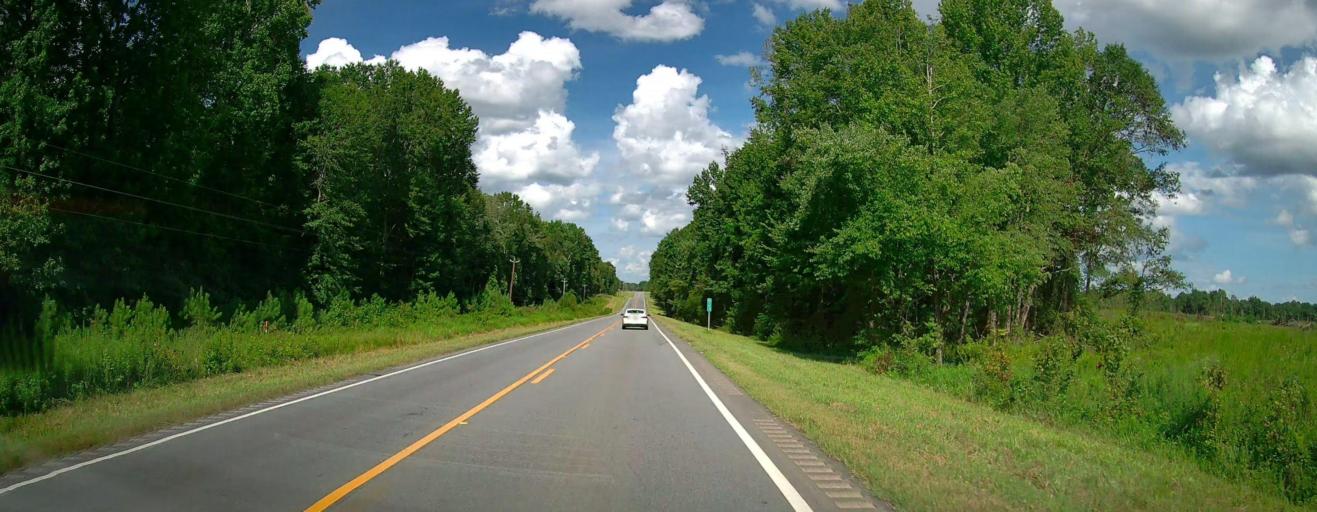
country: US
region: Alabama
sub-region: Lee County
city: Auburn
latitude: 32.4370
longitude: -85.3906
